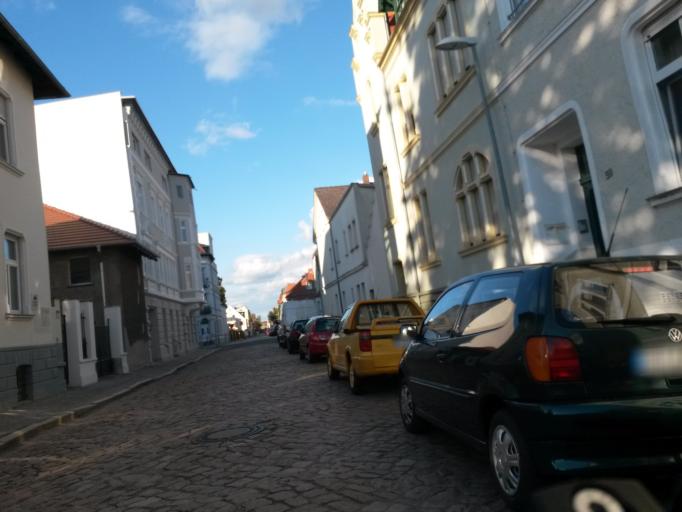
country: DE
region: Saxony-Anhalt
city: Tangermunde
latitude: 52.5439
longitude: 11.9697
